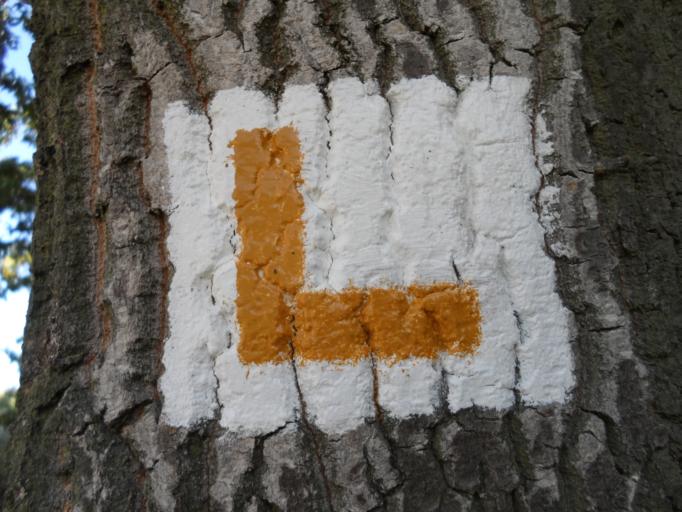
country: HU
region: Veszprem
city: Ajka
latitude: 47.2276
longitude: 17.5559
